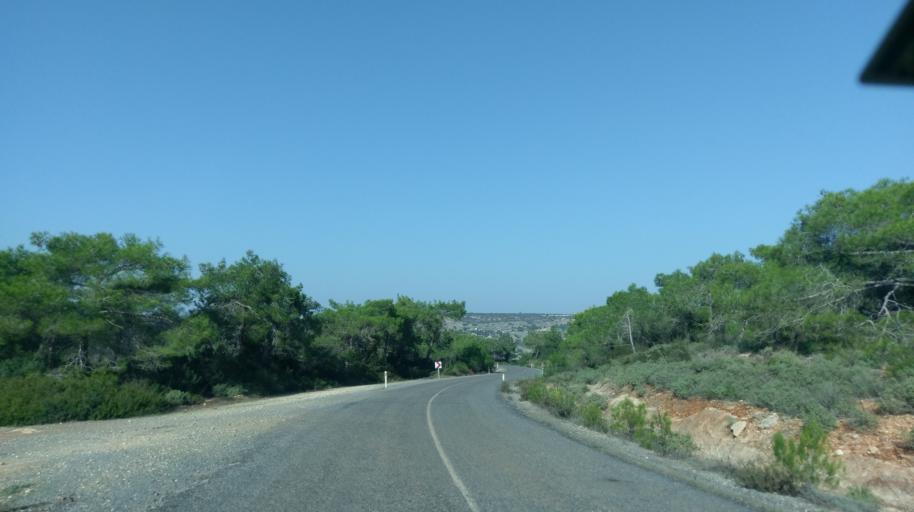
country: CY
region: Ammochostos
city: Leonarisso
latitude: 35.5019
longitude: 34.1948
